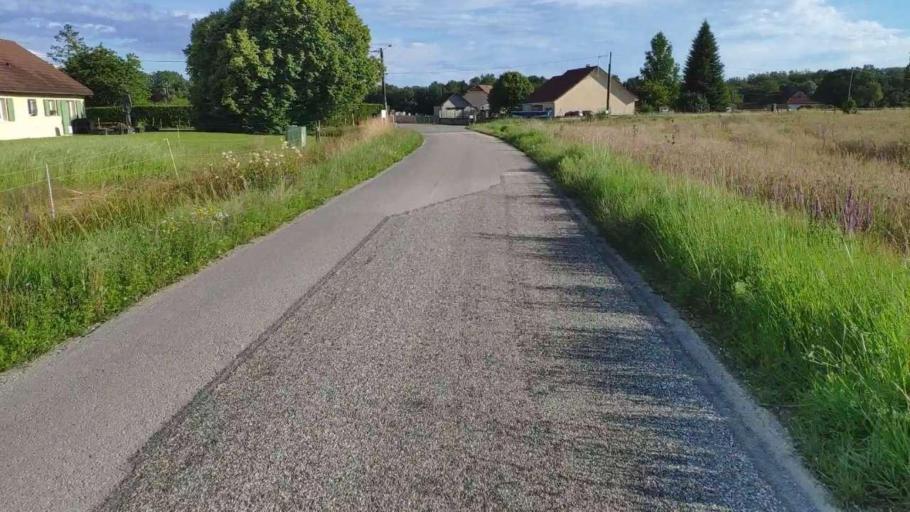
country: FR
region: Franche-Comte
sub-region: Departement du Jura
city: Bletterans
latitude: 46.7829
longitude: 5.4810
